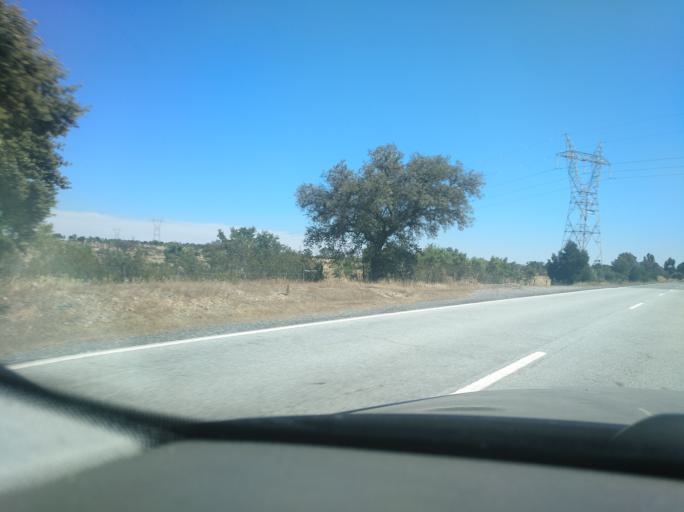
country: PT
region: Beja
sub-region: Castro Verde
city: Castro Verde
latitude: 37.6379
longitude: -8.0817
